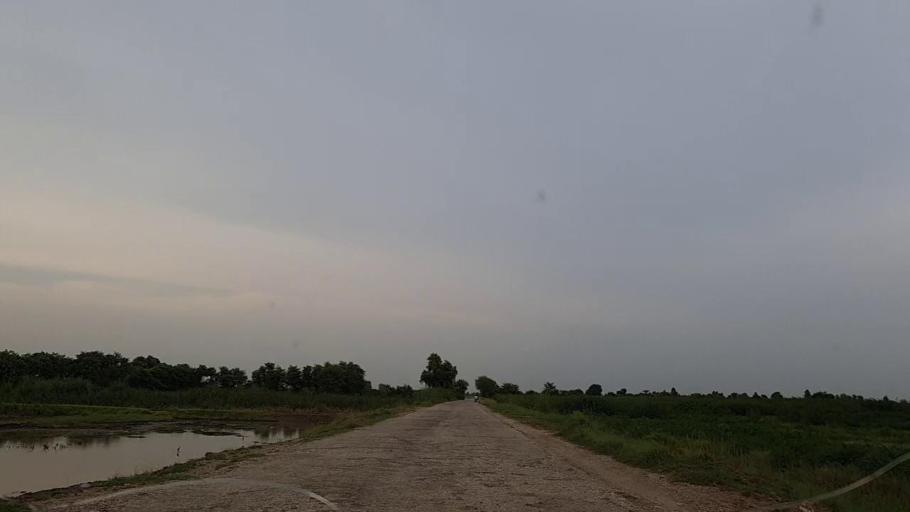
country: PK
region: Sindh
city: Mirpur Mathelo
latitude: 27.8813
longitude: 69.6379
